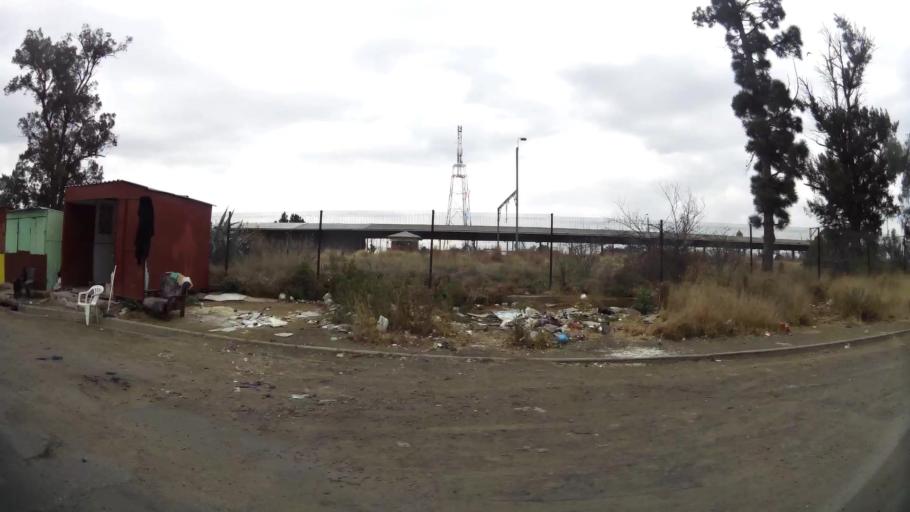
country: ZA
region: Orange Free State
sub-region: Fezile Dabi District Municipality
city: Kroonstad
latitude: -27.6600
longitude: 27.2351
